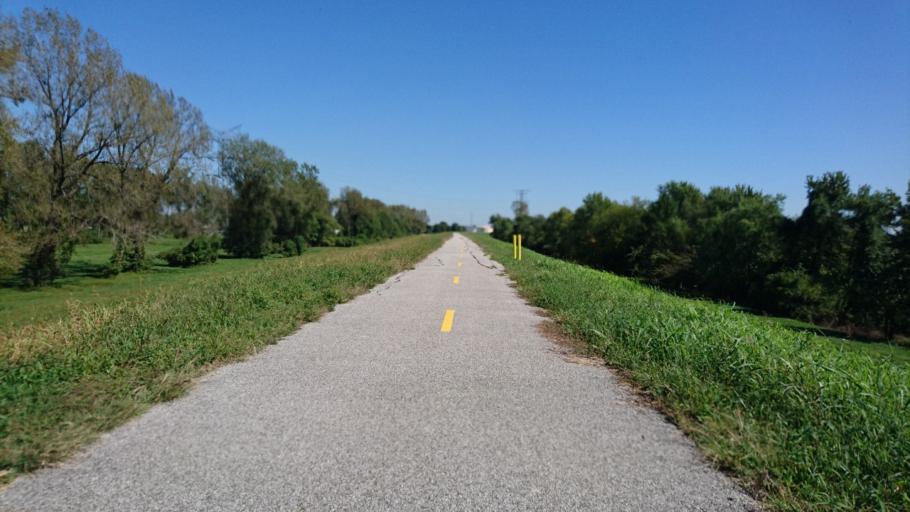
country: US
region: Illinois
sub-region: Madison County
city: Wood River
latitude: 38.8558
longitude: -90.1126
